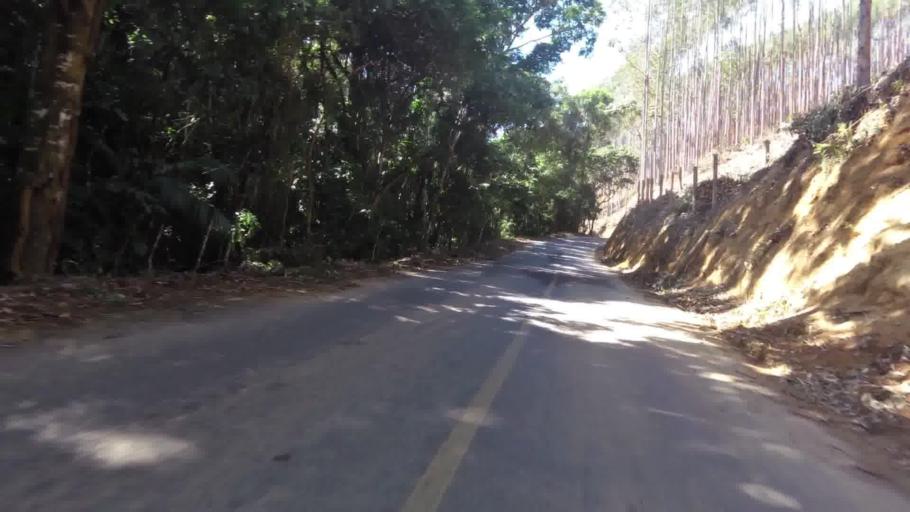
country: BR
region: Espirito Santo
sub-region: Vargem Alta
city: Vargem Alta
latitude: -20.4558
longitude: -40.9161
